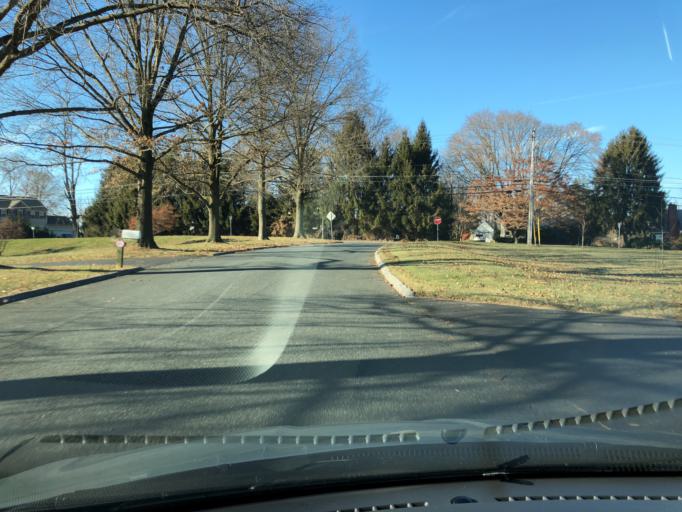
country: US
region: Maryland
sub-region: Baltimore County
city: Kingsville
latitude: 39.4626
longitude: -76.4504
